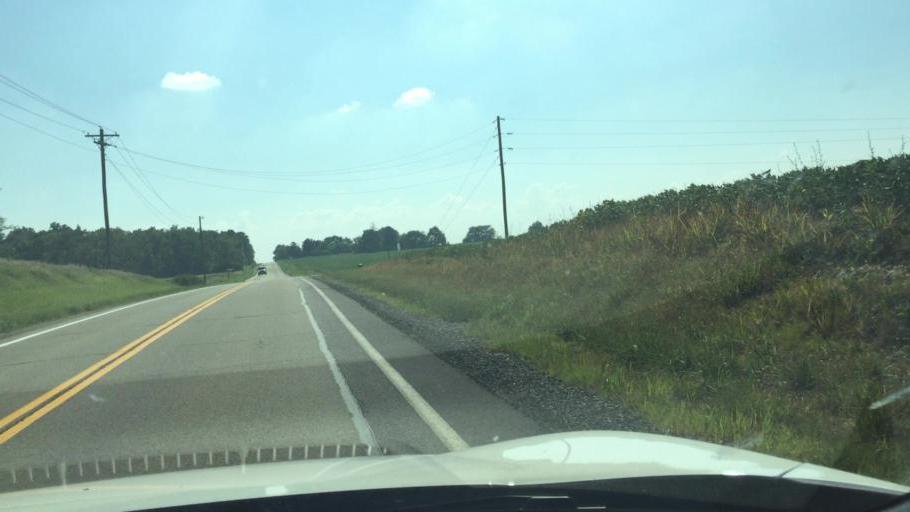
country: US
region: Ohio
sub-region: Champaign County
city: Mechanicsburg
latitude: 40.0880
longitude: -83.6119
